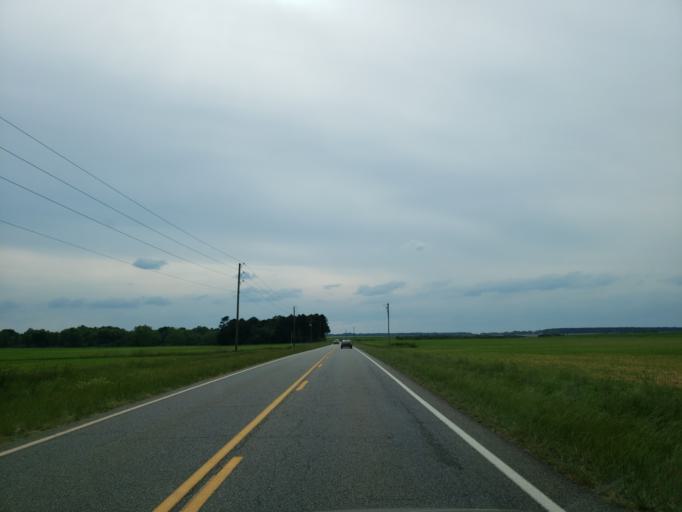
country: US
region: Georgia
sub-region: Macon County
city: Marshallville
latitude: 32.3664
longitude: -83.9101
